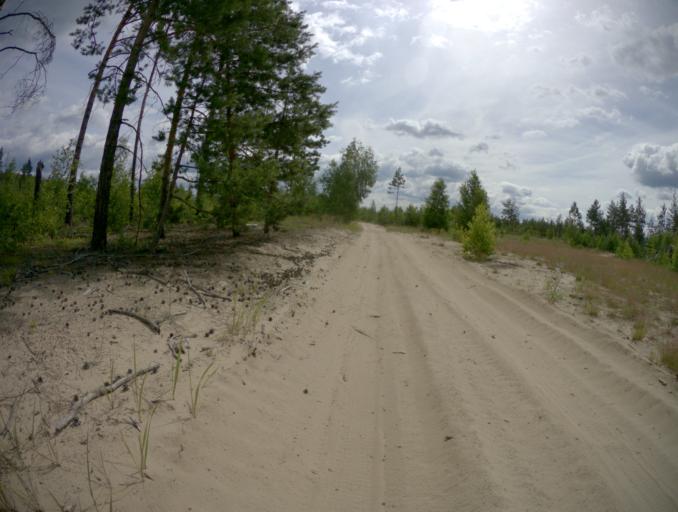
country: RU
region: Nizjnij Novgorod
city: Frolishchi
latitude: 56.5100
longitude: 42.5140
